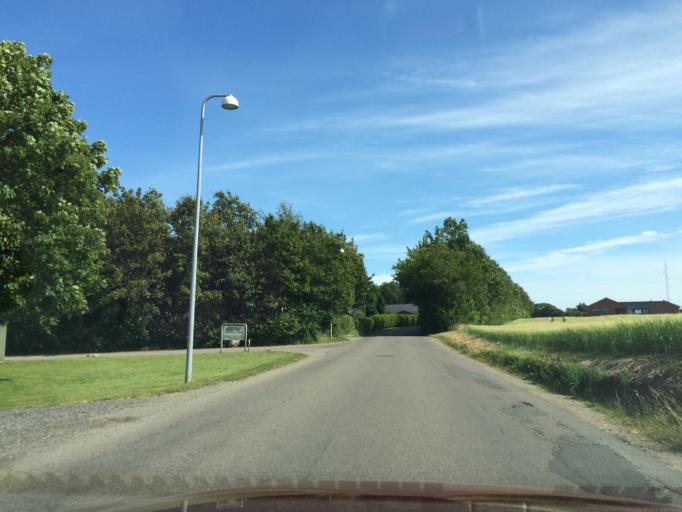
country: DK
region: Central Jutland
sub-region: Silkeborg Kommune
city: Silkeborg
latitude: 56.2191
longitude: 9.5599
